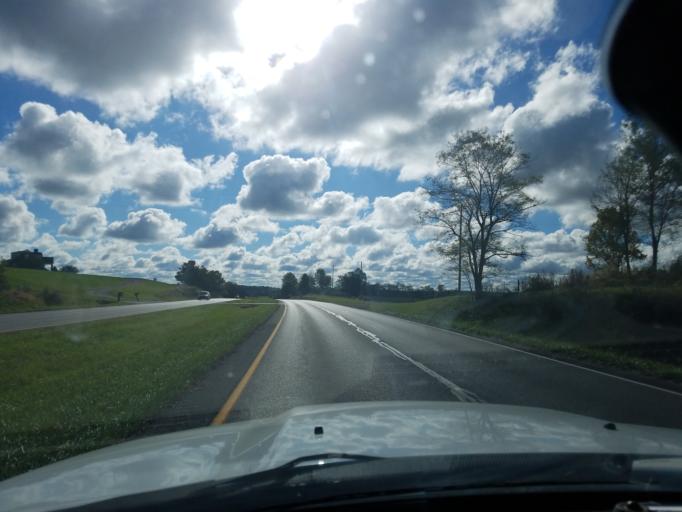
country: US
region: Kentucky
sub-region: Boyle County
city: Junction City
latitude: 37.5900
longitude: -84.7224
